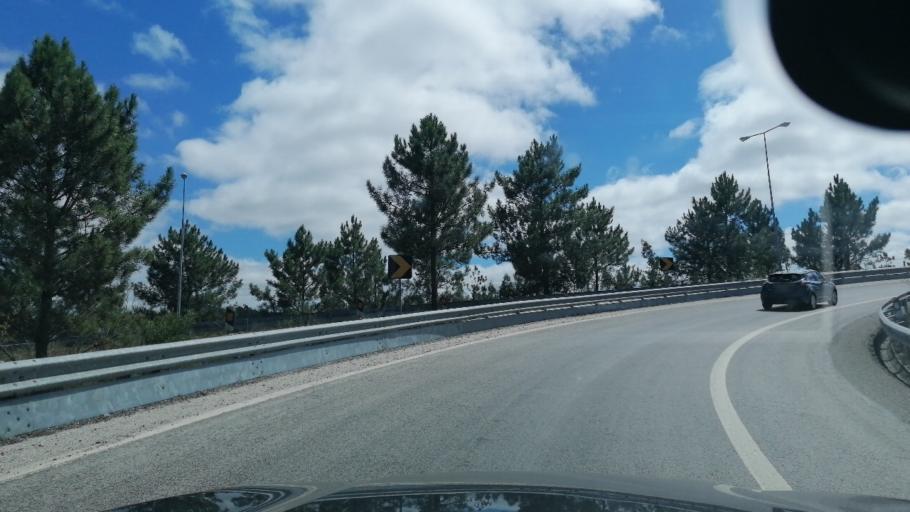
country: PT
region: Leiria
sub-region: Leiria
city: Maceira
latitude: 39.7424
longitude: -8.8704
